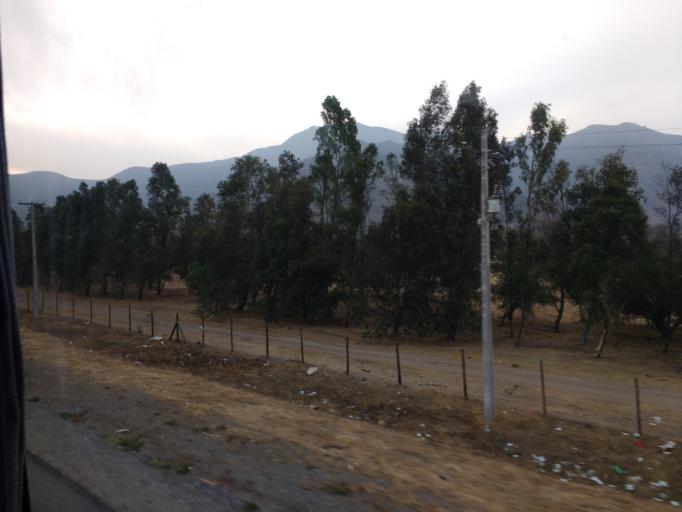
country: CL
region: Santiago Metropolitan
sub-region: Provincia de Talagante
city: Penaflor
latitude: -33.4580
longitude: -70.9071
